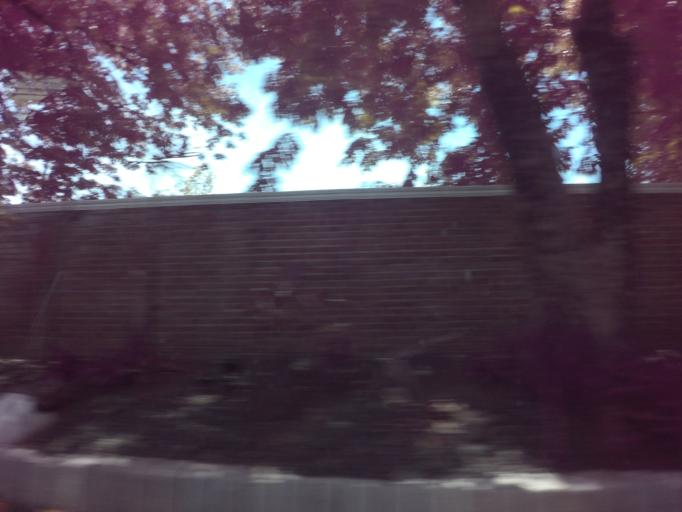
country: PH
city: Sambayanihan People's Village
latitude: 14.4848
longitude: 121.0383
